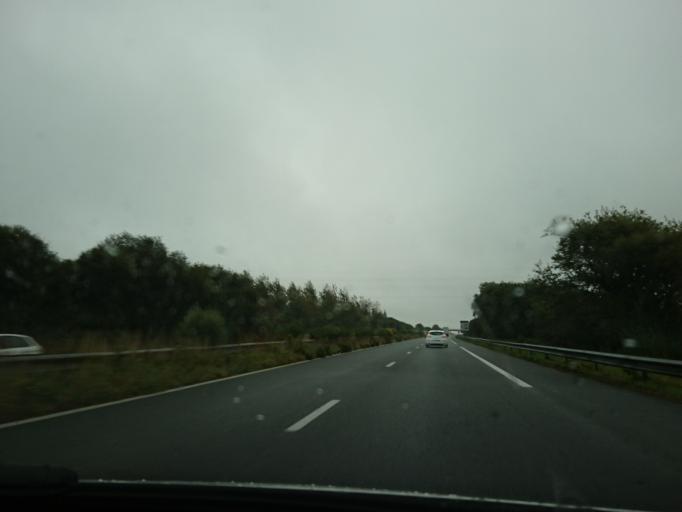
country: FR
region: Brittany
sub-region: Departement du Finistere
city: Mellac
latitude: 47.8723
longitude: -3.6032
